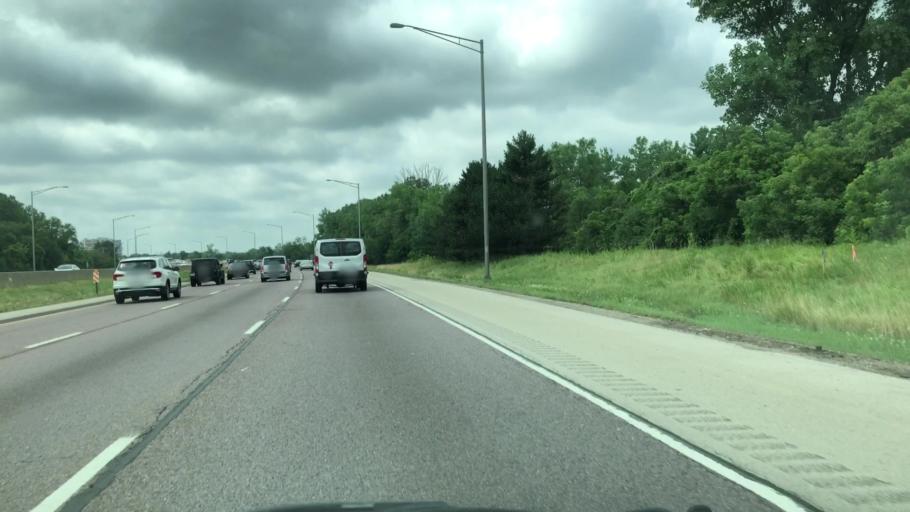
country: US
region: Illinois
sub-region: DuPage County
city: Addison
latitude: 41.9373
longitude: -87.9824
